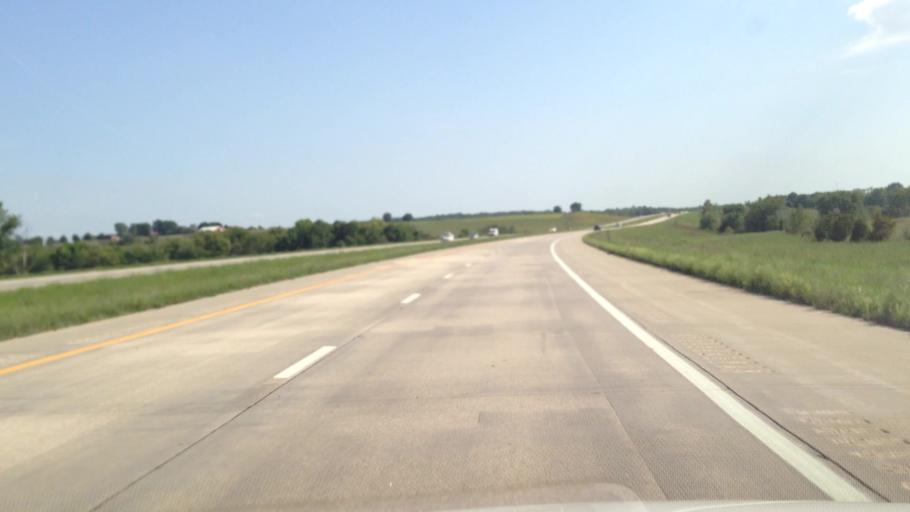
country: US
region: Kansas
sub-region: Miami County
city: Louisburg
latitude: 38.5450
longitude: -94.6858
